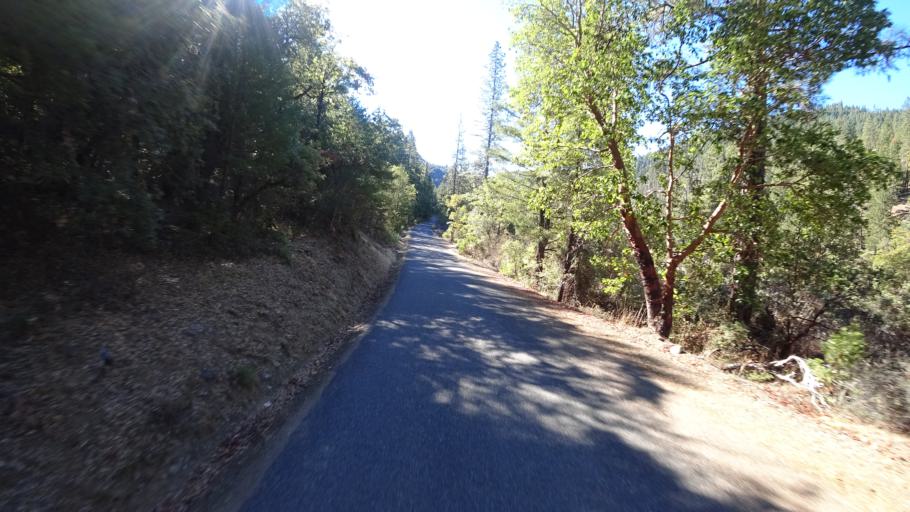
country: US
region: California
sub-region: Humboldt County
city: Willow Creek
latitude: 41.1928
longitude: -123.2159
